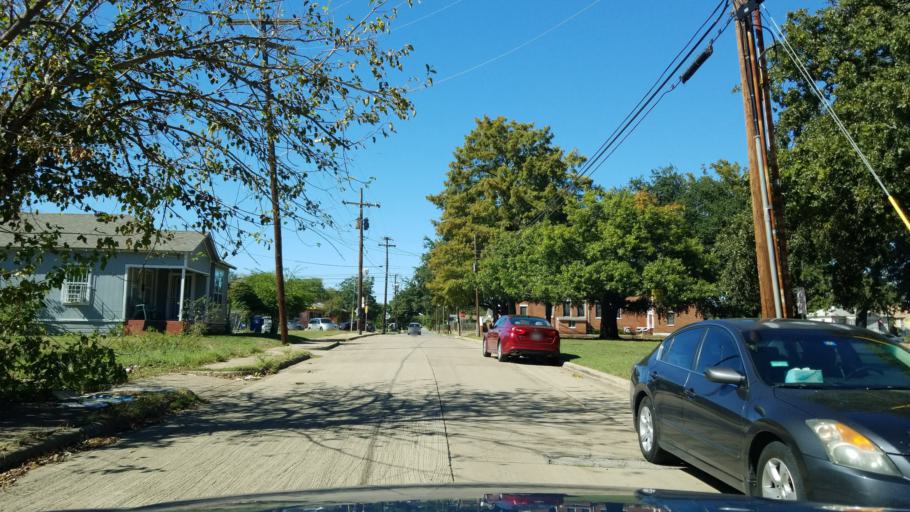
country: US
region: Texas
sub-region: Dallas County
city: Dallas
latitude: 32.7733
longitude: -96.7427
